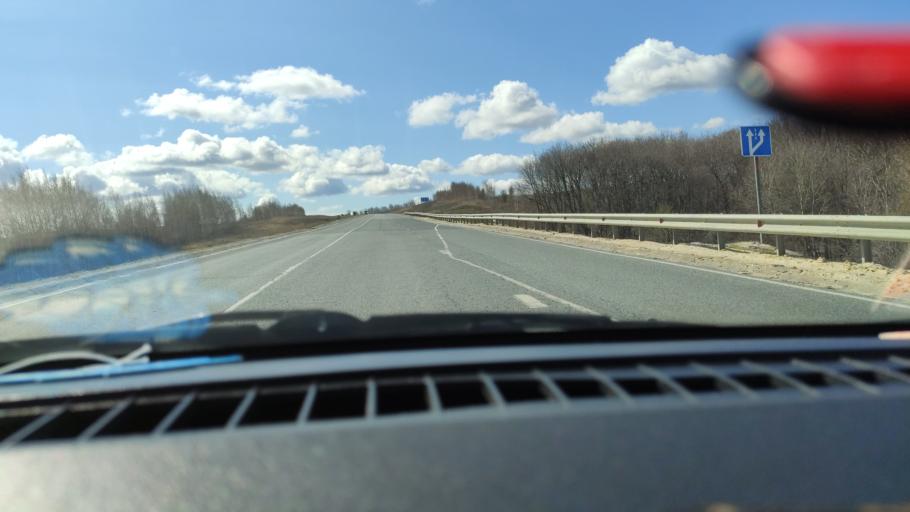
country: RU
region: Samara
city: Syzran'
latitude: 52.9610
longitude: 48.3067
